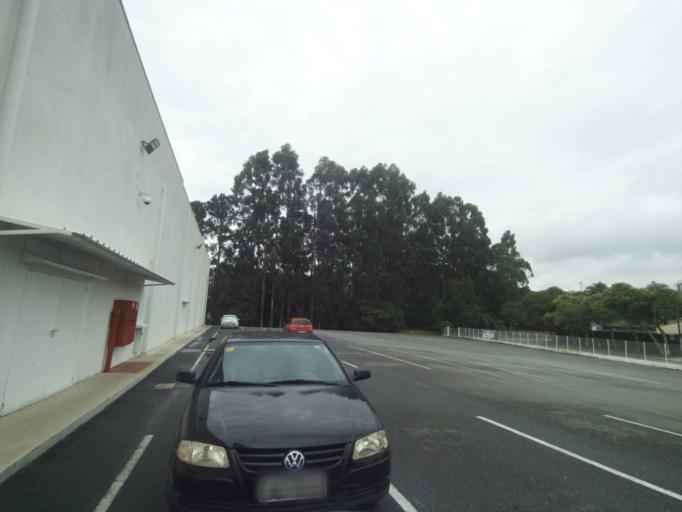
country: BR
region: Parana
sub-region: Curitiba
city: Curitiba
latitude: -25.4331
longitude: -49.3109
